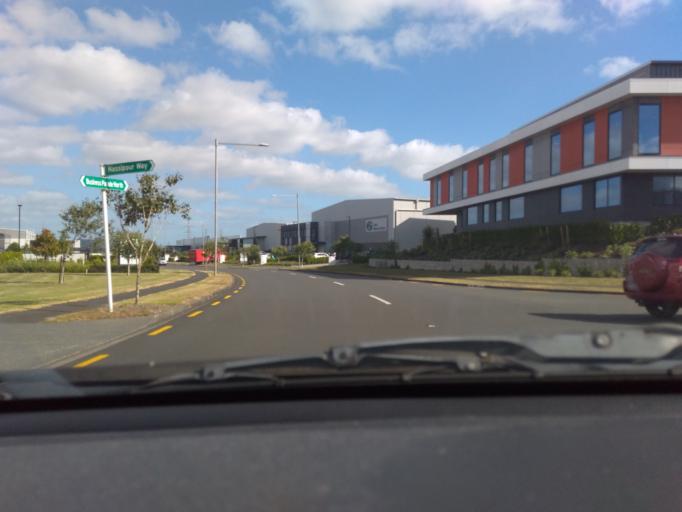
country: NZ
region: Auckland
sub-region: Auckland
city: Tamaki
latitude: -36.9336
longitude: 174.8766
